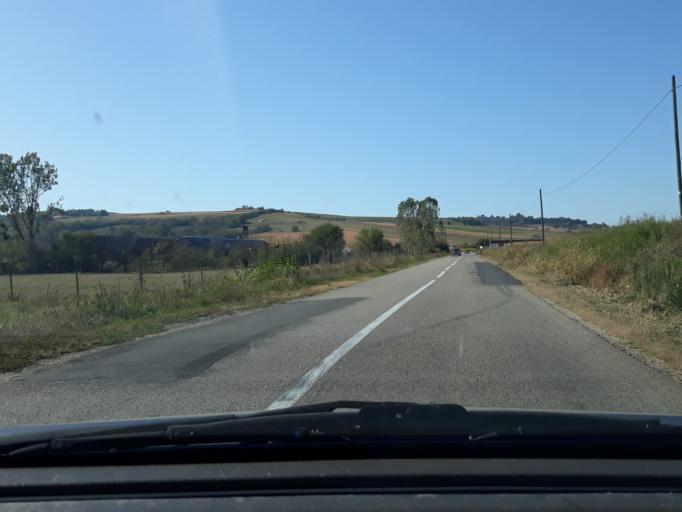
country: RO
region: Salaj
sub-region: Comuna Dobrin
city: Dobrin
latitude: 47.3019
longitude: 23.1283
